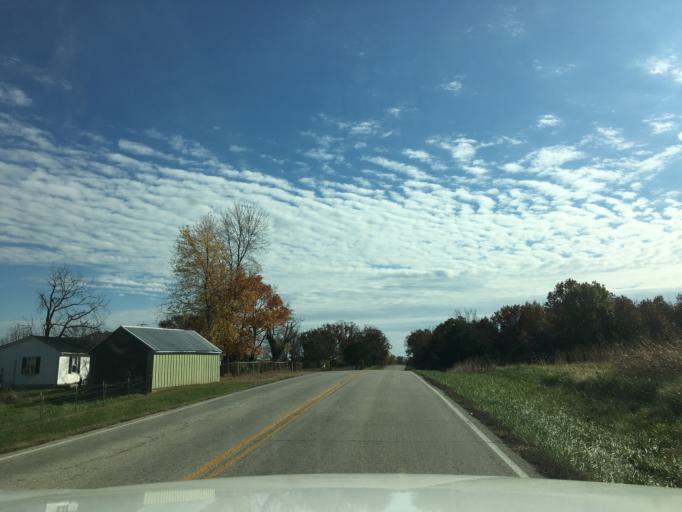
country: US
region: Missouri
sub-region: Maries County
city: Belle
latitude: 38.3546
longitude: -91.8004
